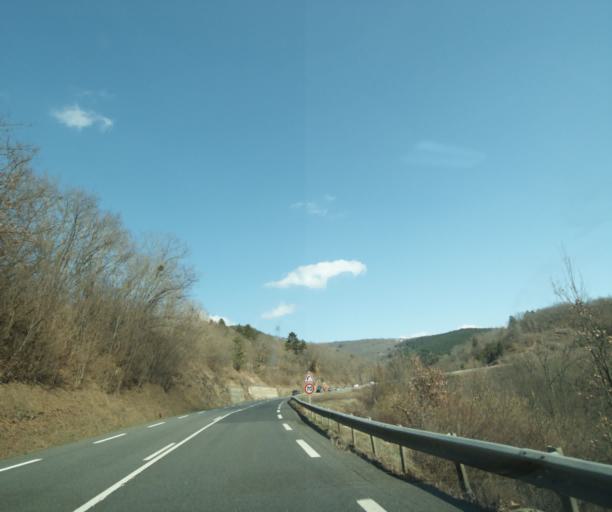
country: FR
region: Languedoc-Roussillon
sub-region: Departement de la Lozere
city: Mende
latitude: 44.5371
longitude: 3.5628
